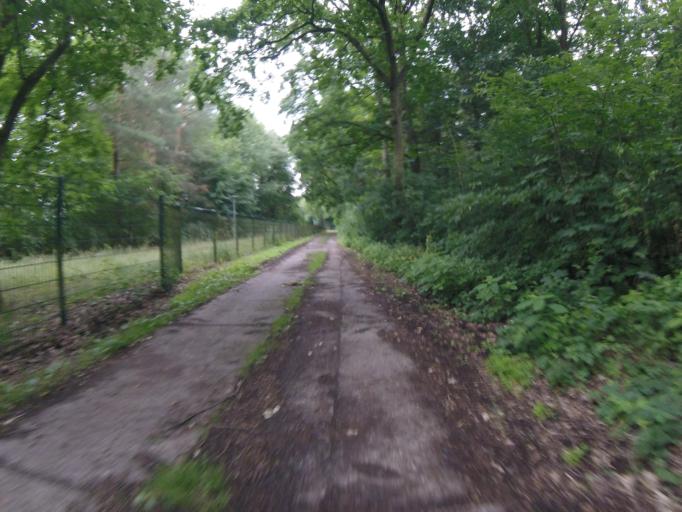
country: DE
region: Brandenburg
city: Konigs Wusterhausen
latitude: 52.2987
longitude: 13.6414
